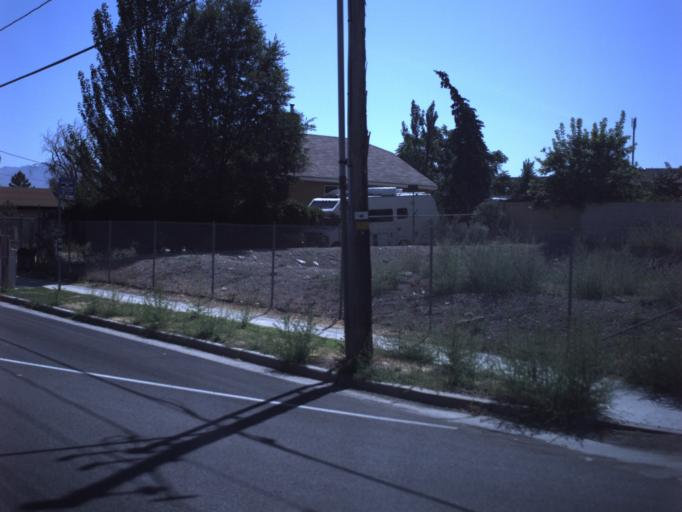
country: US
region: Utah
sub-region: Salt Lake County
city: Magna
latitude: 40.6965
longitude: -112.0803
